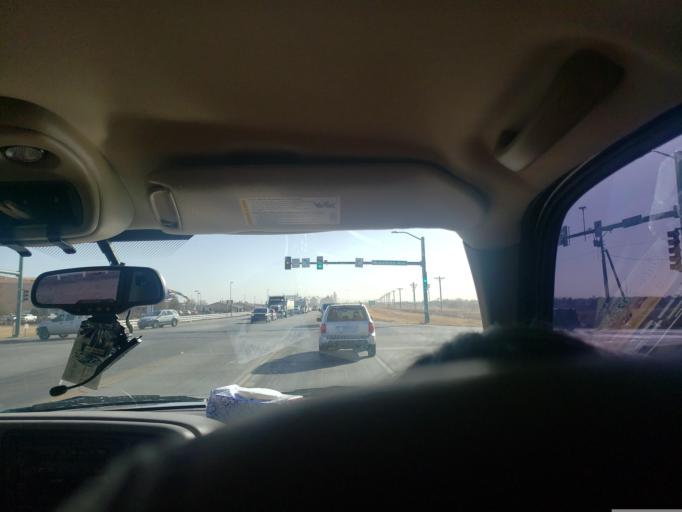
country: US
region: Kansas
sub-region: Finney County
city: Garden City
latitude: 37.9755
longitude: -100.8385
